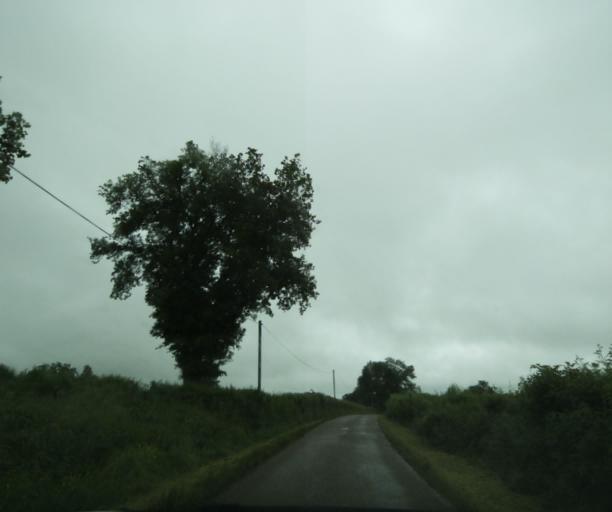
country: FR
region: Bourgogne
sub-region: Departement de Saone-et-Loire
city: Charolles
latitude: 46.3560
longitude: 4.2302
